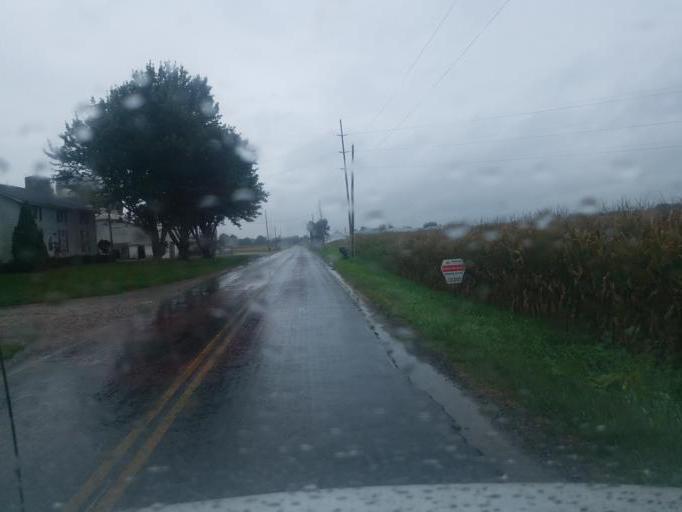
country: US
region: Ohio
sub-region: Medina County
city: Seville
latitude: 40.9934
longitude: -81.8569
